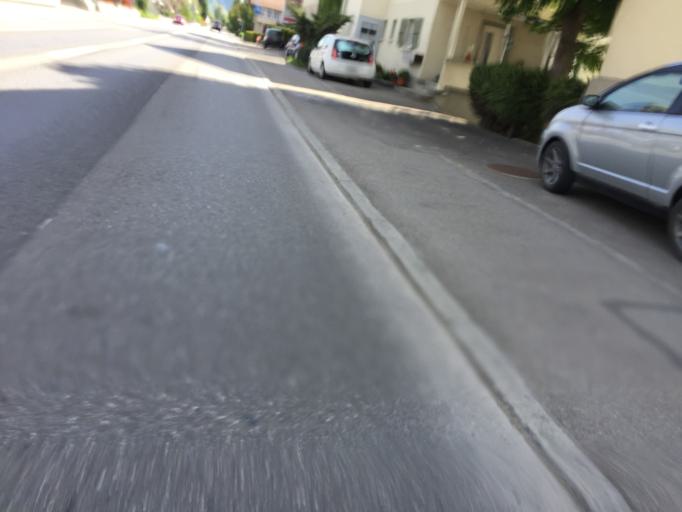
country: CH
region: Bern
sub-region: Bern-Mittelland District
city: Konolfingen
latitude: 46.8805
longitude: 7.6232
